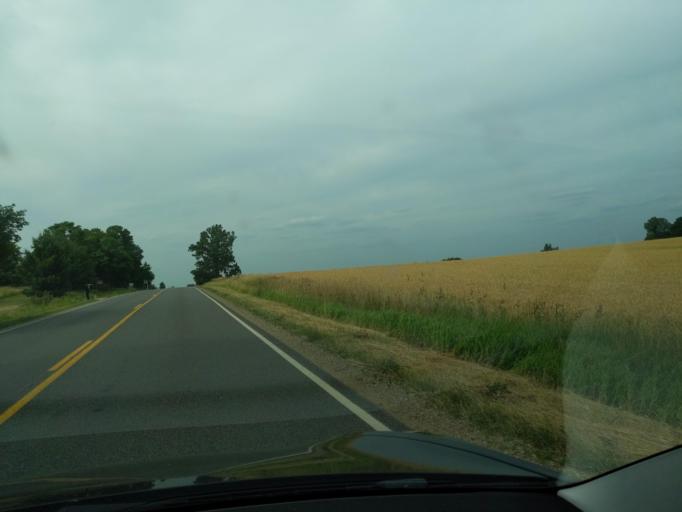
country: US
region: Michigan
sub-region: Clinton County
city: DeWitt
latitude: 42.8619
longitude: -84.6025
